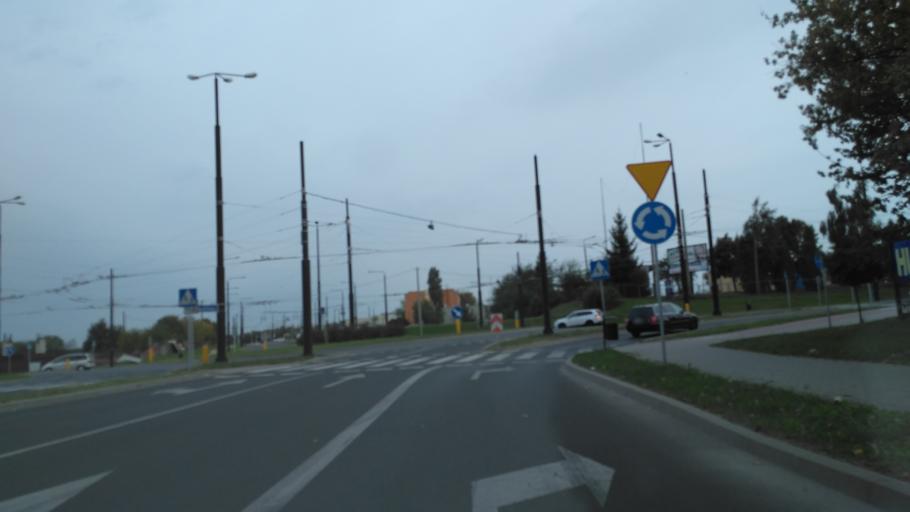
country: PL
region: Lublin Voivodeship
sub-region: Powiat lubelski
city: Jakubowice Murowane
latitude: 51.2311
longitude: 22.6215
